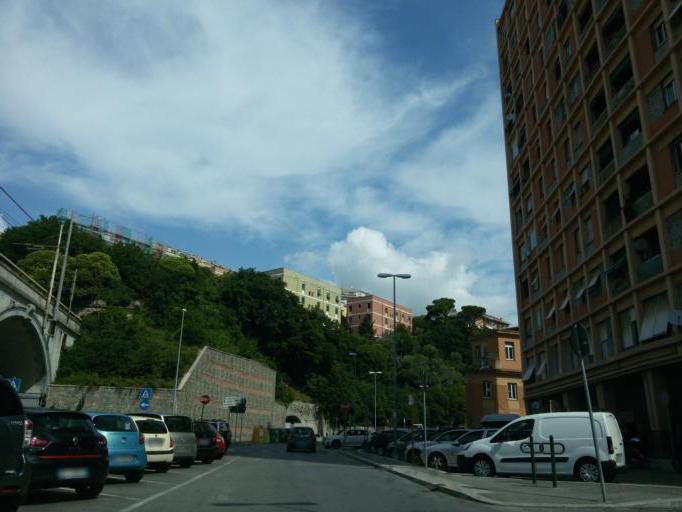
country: IT
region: Liguria
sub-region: Provincia di Genova
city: Genoa
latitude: 44.3955
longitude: 8.9850
